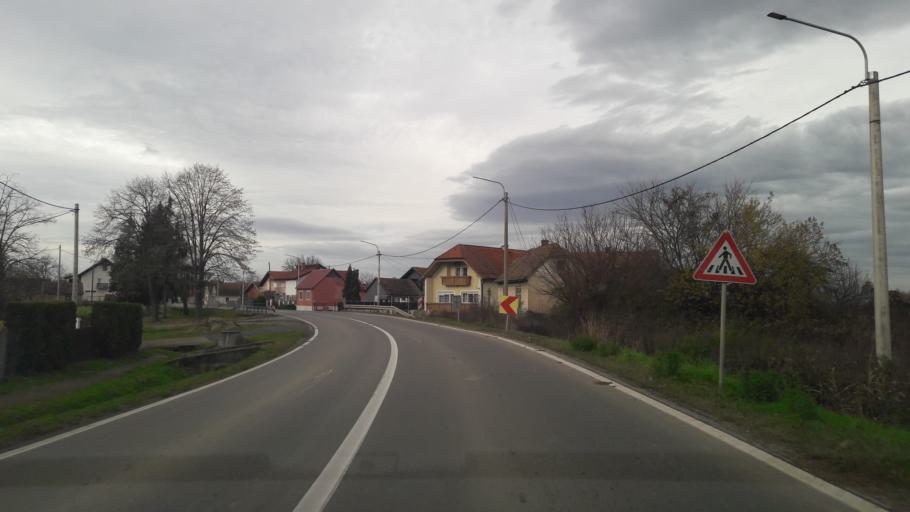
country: HR
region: Osjecko-Baranjska
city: Fericanci
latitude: 45.5233
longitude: 17.9956
